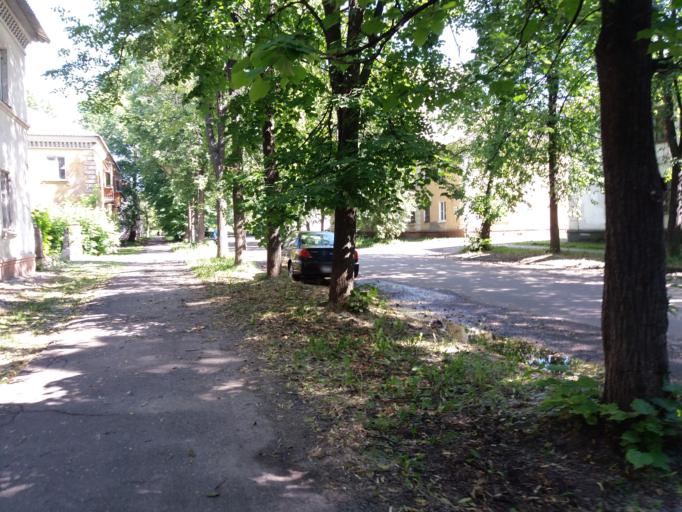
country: RU
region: Jaroslavl
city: Yaroslavl
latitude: 57.6411
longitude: 39.8348
